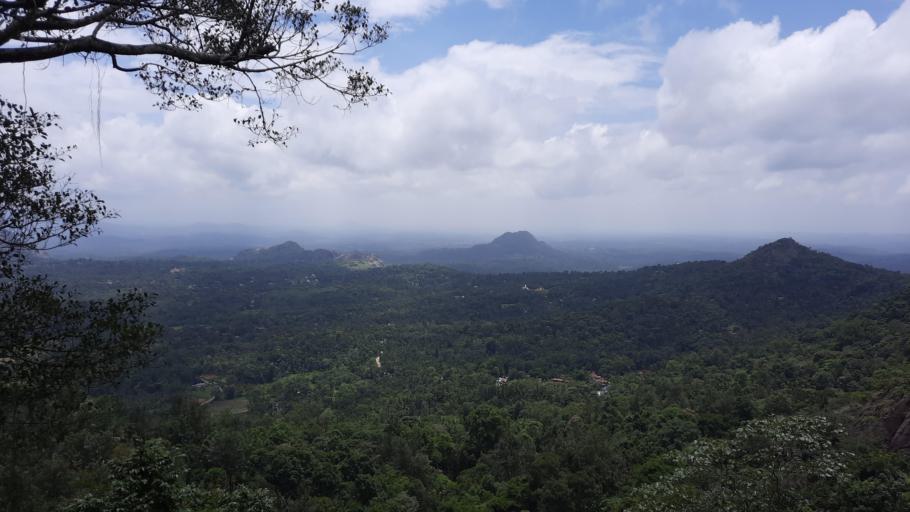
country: IN
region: Kerala
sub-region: Wayanad
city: Kalpetta
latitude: 11.6266
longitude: 76.2356
